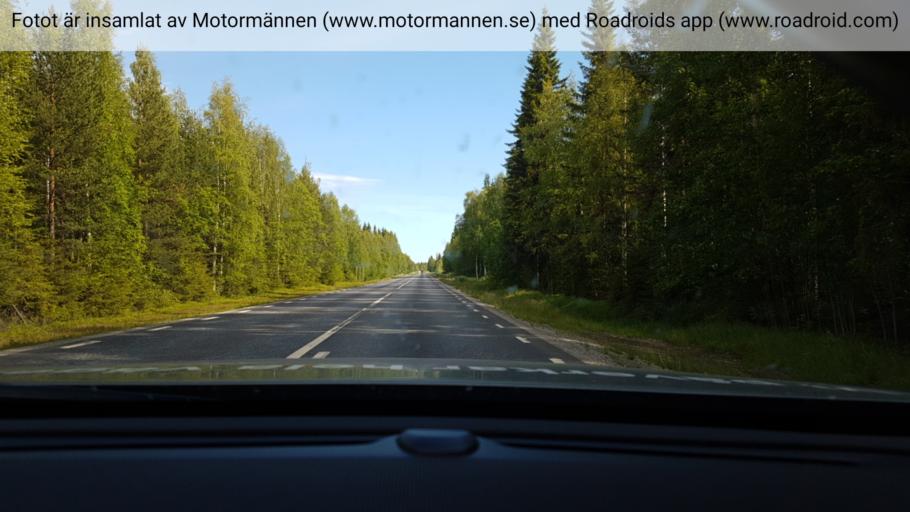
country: SE
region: Vaesterbotten
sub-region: Lycksele Kommun
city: Soderfors
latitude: 64.8252
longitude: 18.0557
